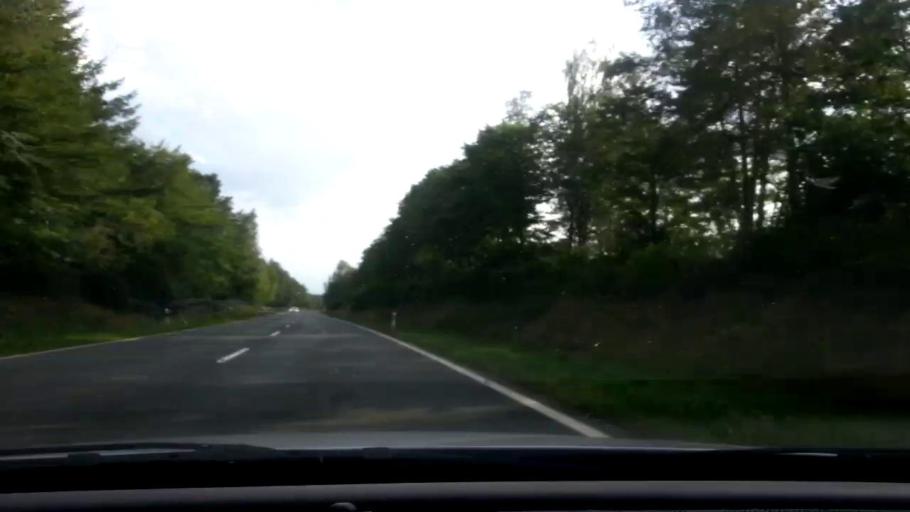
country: DE
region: Bavaria
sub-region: Upper Palatinate
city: Berg
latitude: 49.8538
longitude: 12.1560
